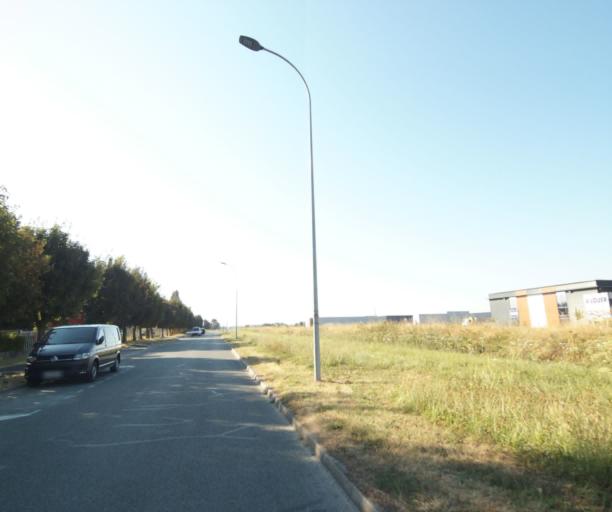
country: FR
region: Ile-de-France
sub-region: Departement de Seine-et-Marne
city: Lieusaint
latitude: 48.6209
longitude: 2.5651
